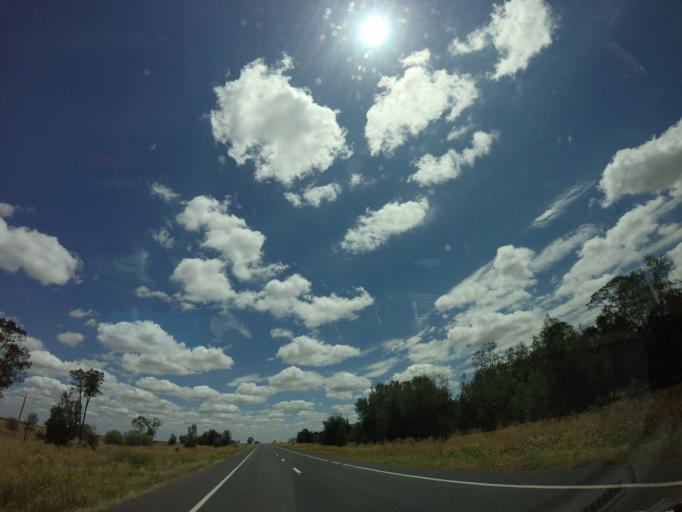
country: AU
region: New South Wales
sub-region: Moree Plains
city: Boggabilla
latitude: -28.9629
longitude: 150.0832
